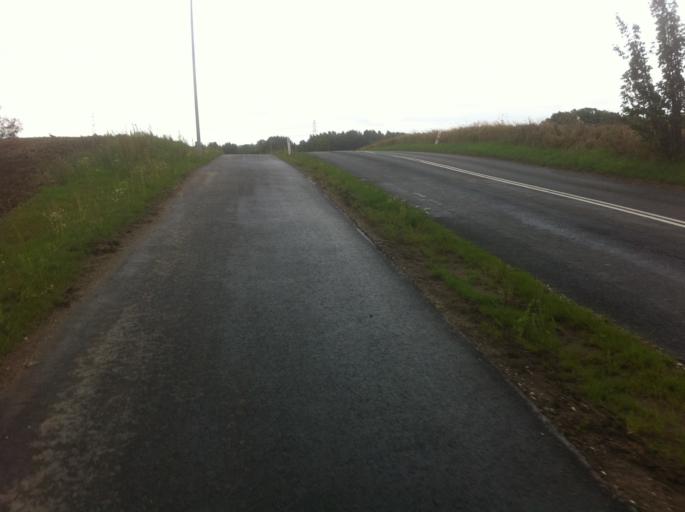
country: DK
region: Capital Region
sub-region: Allerod Kommune
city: Lillerod
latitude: 55.9035
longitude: 12.3425
